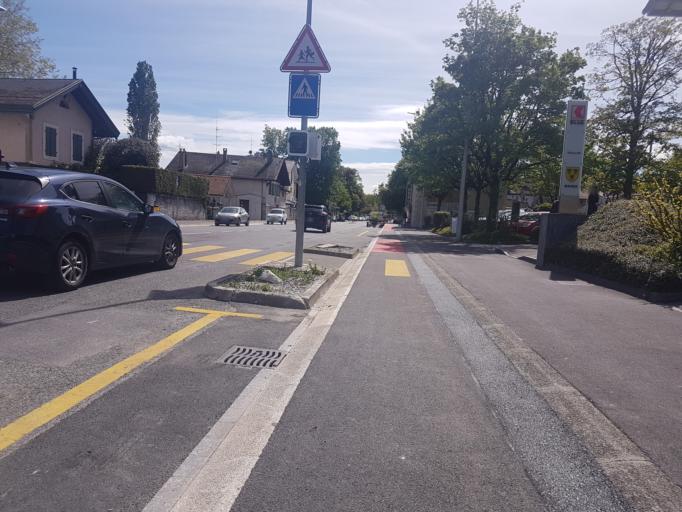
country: CH
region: Geneva
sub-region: Geneva
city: Bellevue
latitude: 46.2548
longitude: 6.1546
